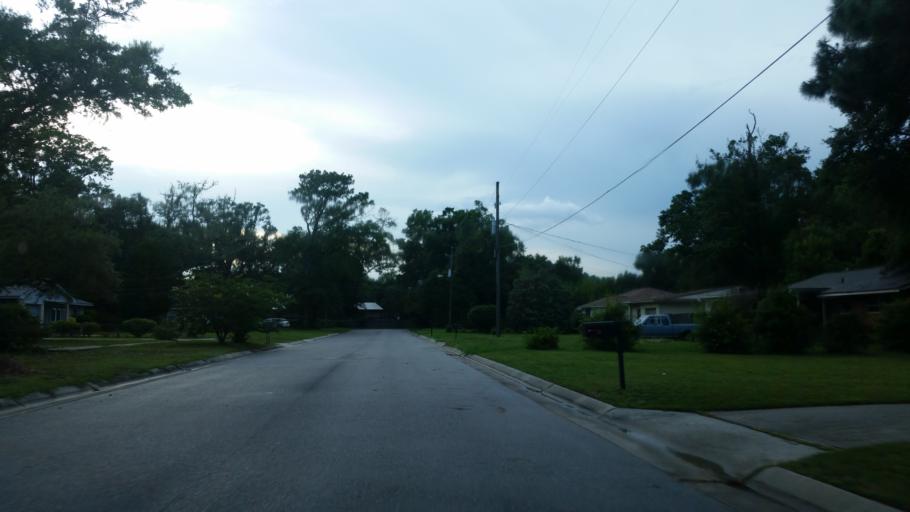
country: US
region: Florida
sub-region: Escambia County
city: Ferry Pass
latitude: 30.4951
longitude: -87.1635
